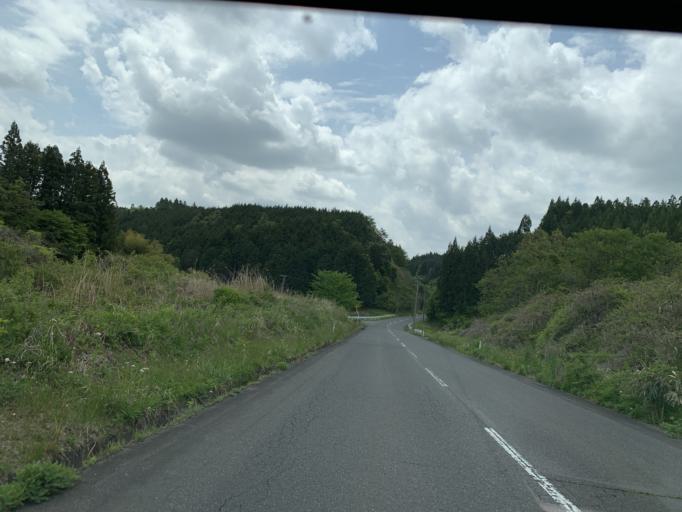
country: JP
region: Miyagi
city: Furukawa
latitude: 38.7157
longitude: 140.9204
